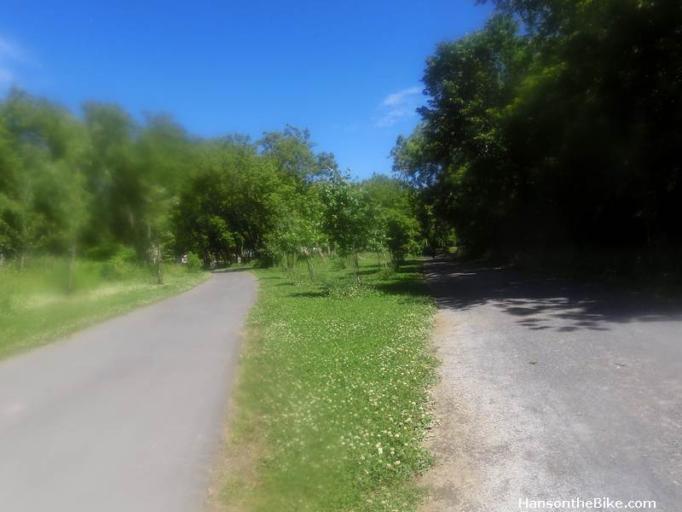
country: CA
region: Ontario
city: Kingston
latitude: 44.2473
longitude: -76.4850
